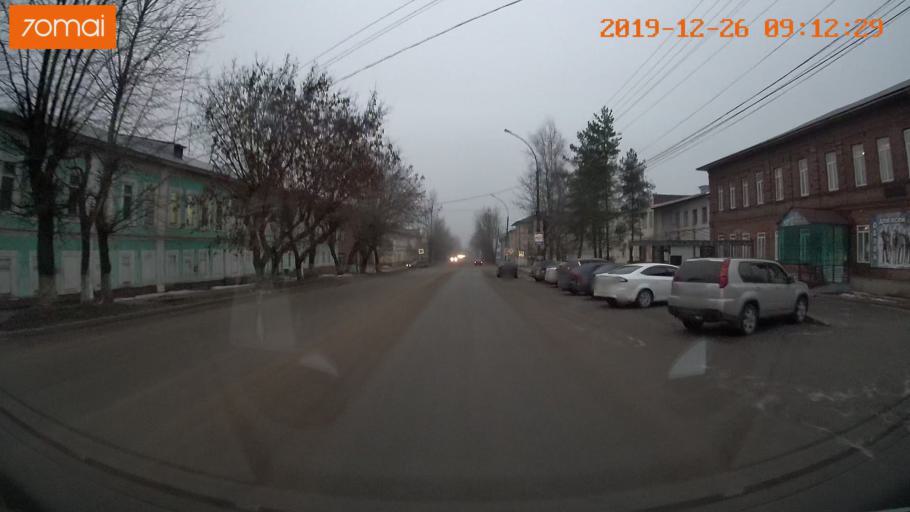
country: RU
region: Vologda
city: Gryazovets
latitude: 58.8814
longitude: 40.2534
